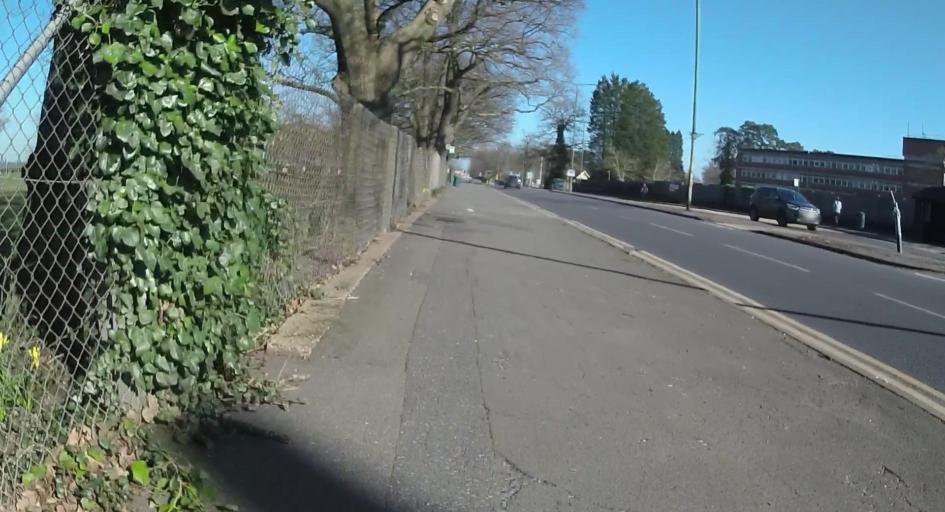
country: GB
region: England
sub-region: Royal Borough of Windsor and Maidenhead
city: Ascot
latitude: 51.4113
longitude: -0.6871
